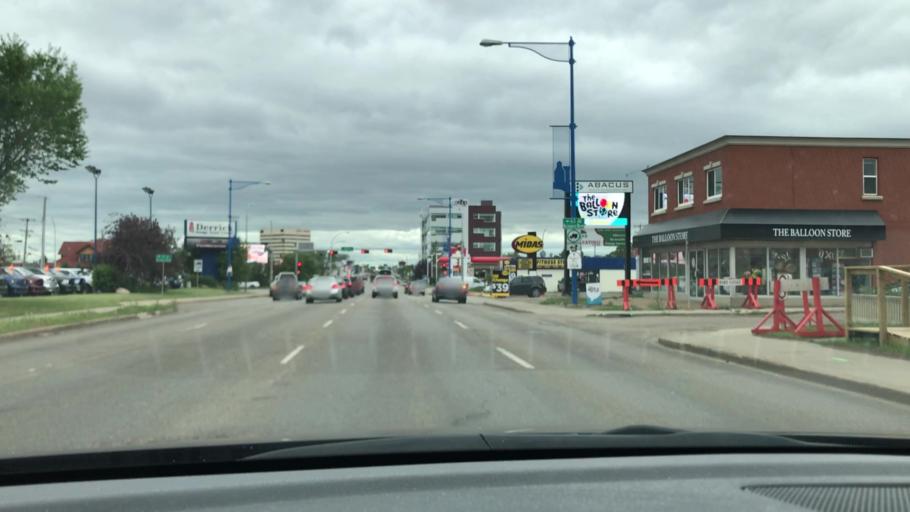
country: CA
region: Alberta
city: Edmonton
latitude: 53.5009
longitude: -113.4977
